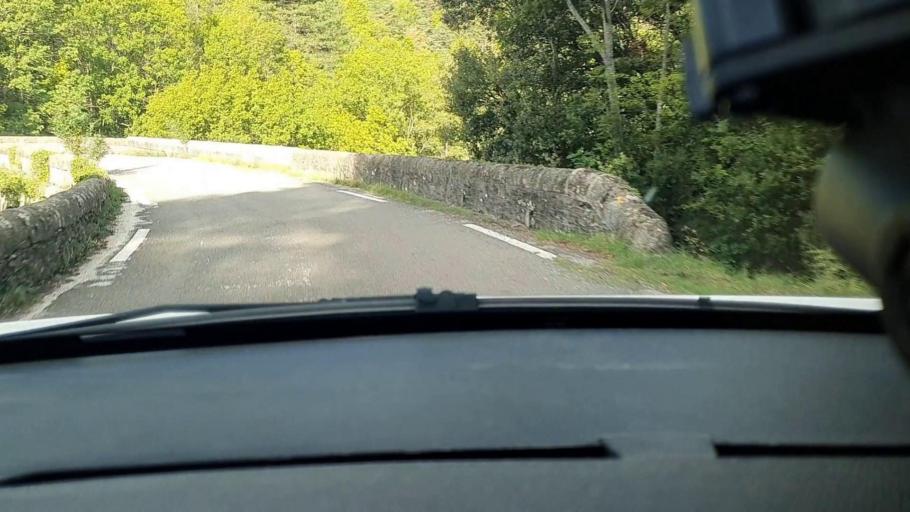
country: FR
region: Languedoc-Roussillon
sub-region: Departement du Gard
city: Besseges
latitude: 44.3668
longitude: 3.9973
